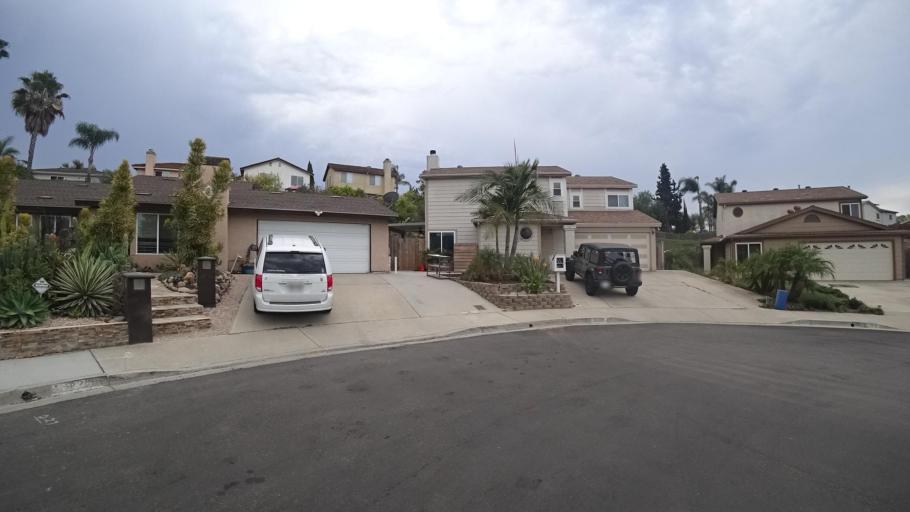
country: US
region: California
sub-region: San Diego County
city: Escondido
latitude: 33.1466
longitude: -117.1149
